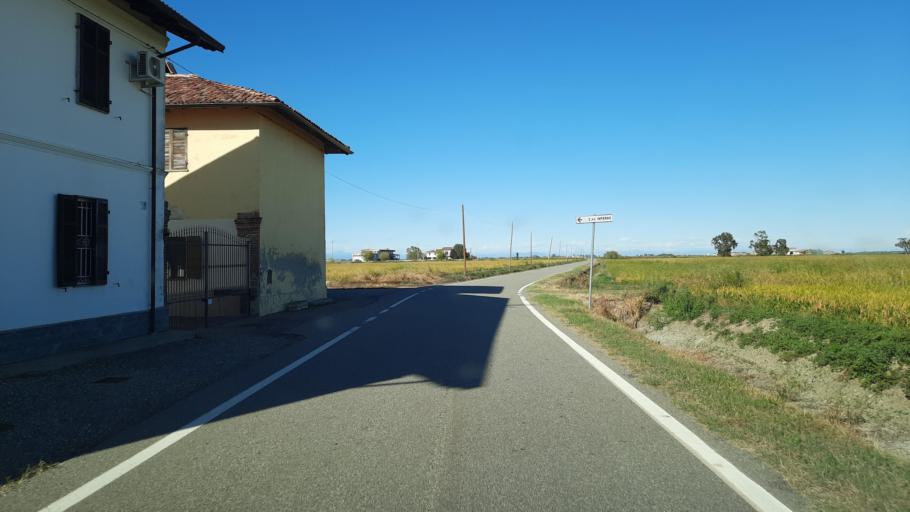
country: IT
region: Piedmont
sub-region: Provincia di Vercelli
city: Ronsecco
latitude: 45.2693
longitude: 8.2946
